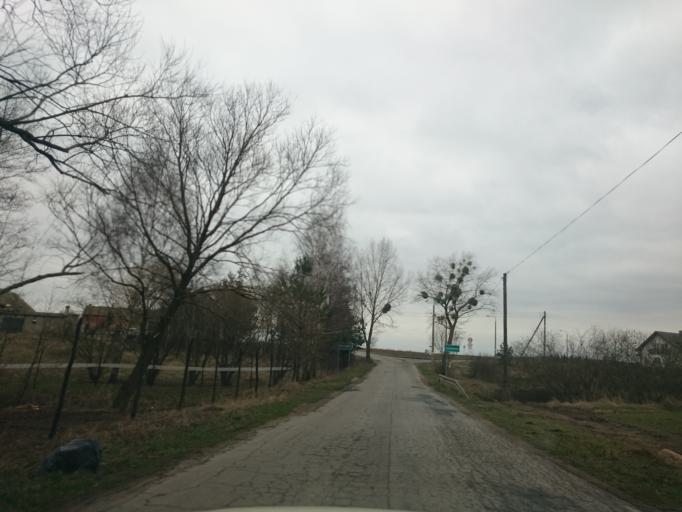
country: PL
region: Kujawsko-Pomorskie
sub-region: Powiat torunski
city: Lubicz Gorny
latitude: 53.0435
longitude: 18.8163
